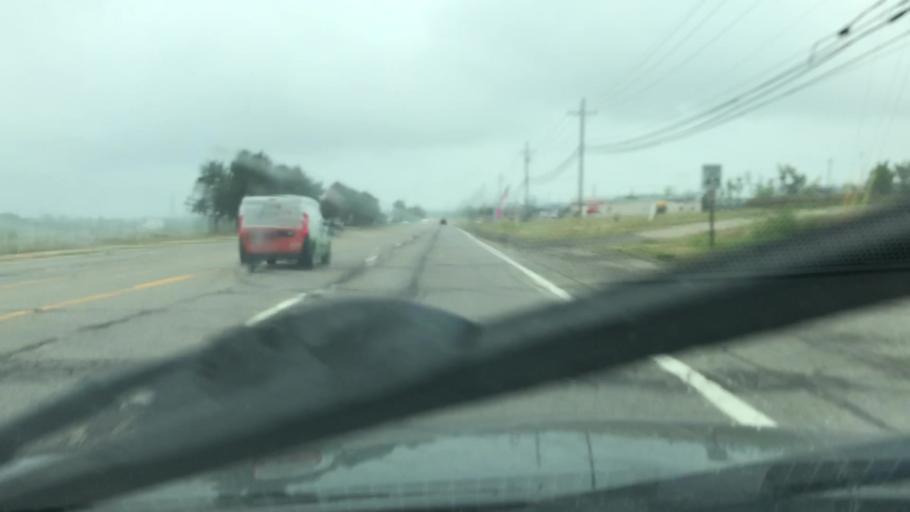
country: US
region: Michigan
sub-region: Oakland County
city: Wixom
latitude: 42.5041
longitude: -83.5364
